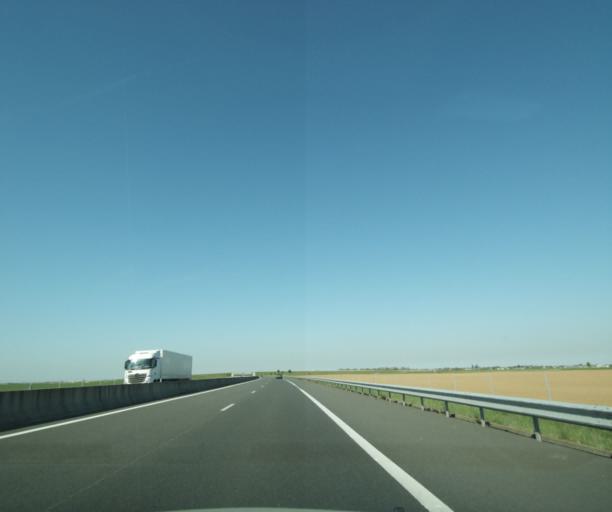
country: FR
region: Centre
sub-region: Departement du Loiret
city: Puiseaux
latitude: 48.0993
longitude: 2.0383
